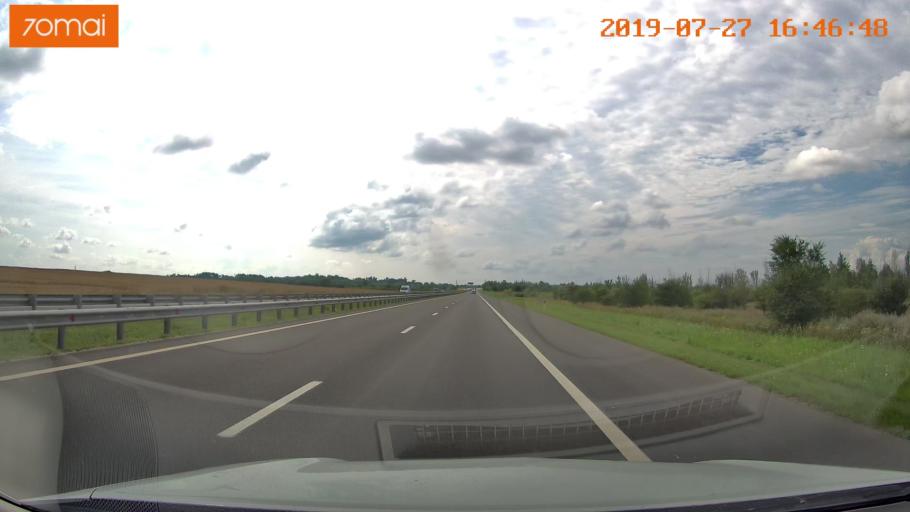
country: RU
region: Kaliningrad
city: Gvardeysk
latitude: 54.6676
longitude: 21.0118
